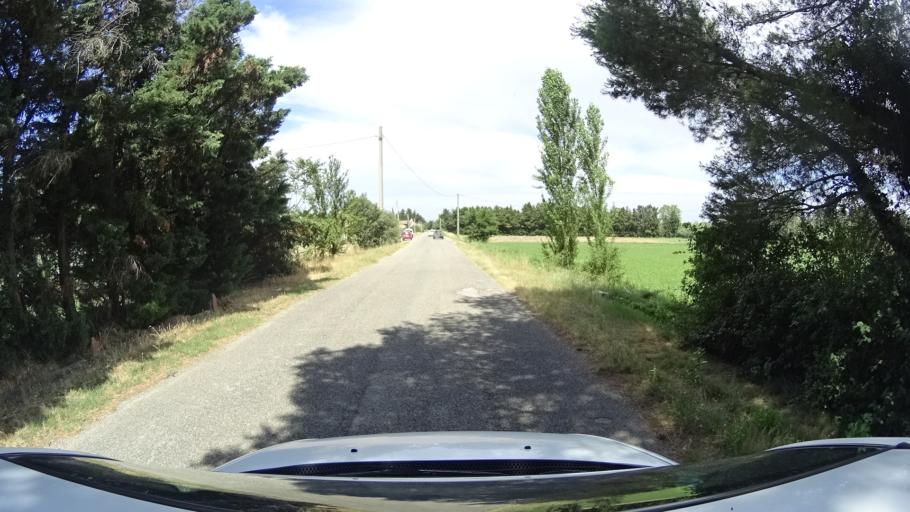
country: FR
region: Provence-Alpes-Cote d'Azur
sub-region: Departement du Vaucluse
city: Cheval-Blanc
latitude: 43.8173
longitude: 5.0621
